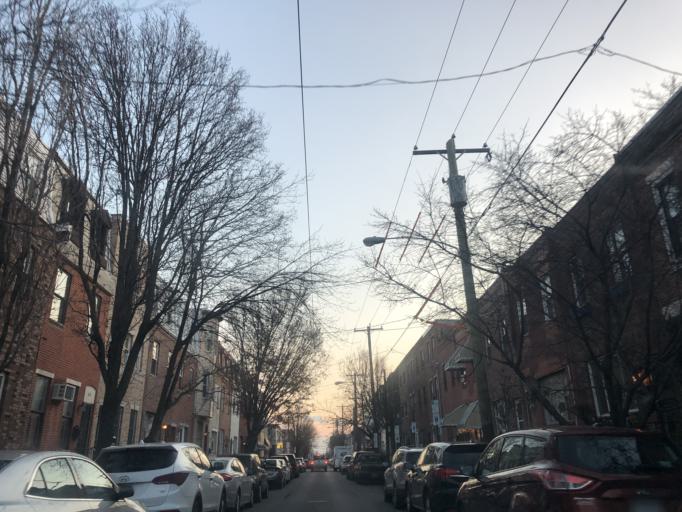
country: US
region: Pennsylvania
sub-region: Philadelphia County
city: Philadelphia
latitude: 39.9272
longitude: -75.1653
